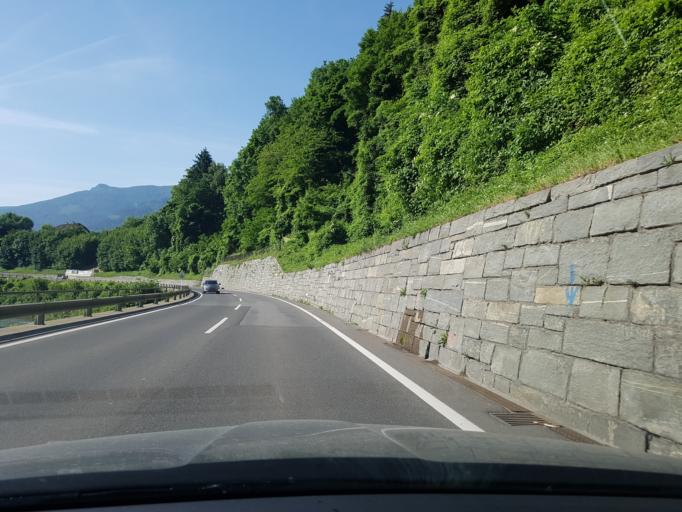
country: AT
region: Carinthia
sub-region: Politischer Bezirk Spittal an der Drau
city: Spittal an der Drau
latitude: 46.8041
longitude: 13.4956
